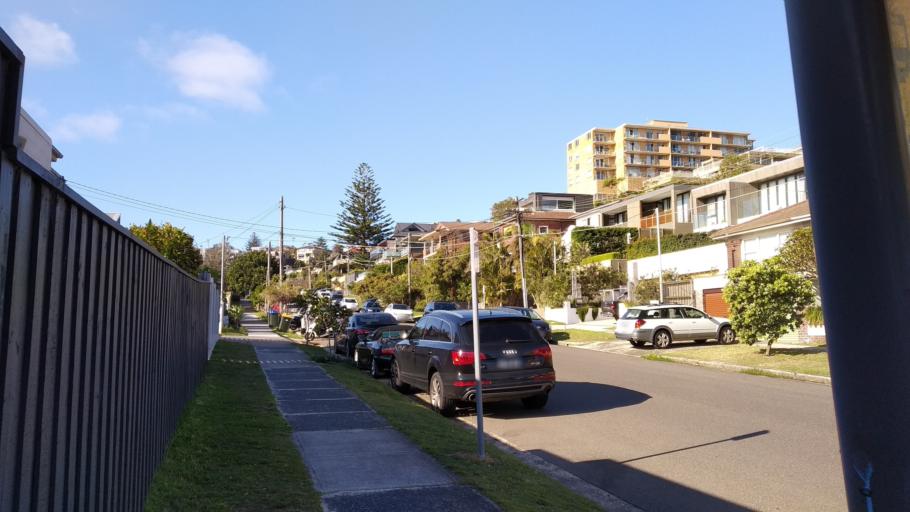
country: AU
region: New South Wales
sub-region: Waverley
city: North Bondi
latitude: -33.8845
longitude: 151.2808
